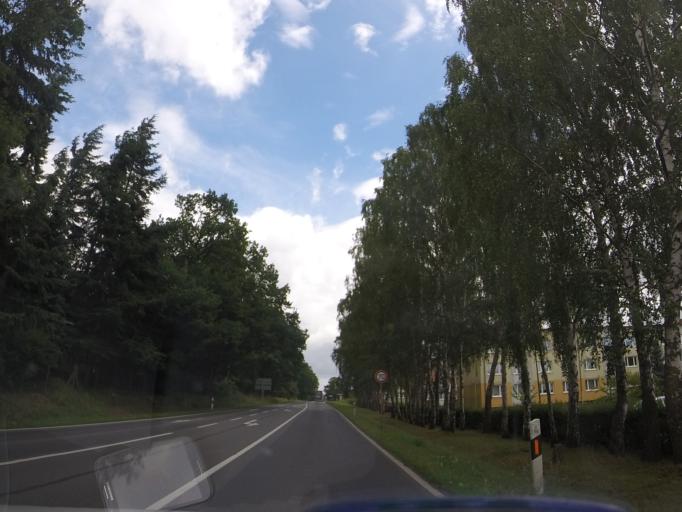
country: DE
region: Mecklenburg-Vorpommern
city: Lalendorf
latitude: 53.7596
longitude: 12.3870
